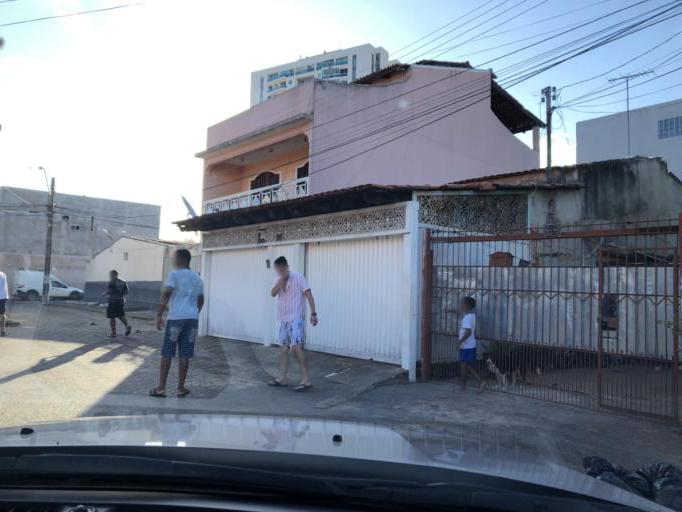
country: BR
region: Federal District
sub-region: Brasilia
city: Brasilia
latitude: -15.8532
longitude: -48.0366
